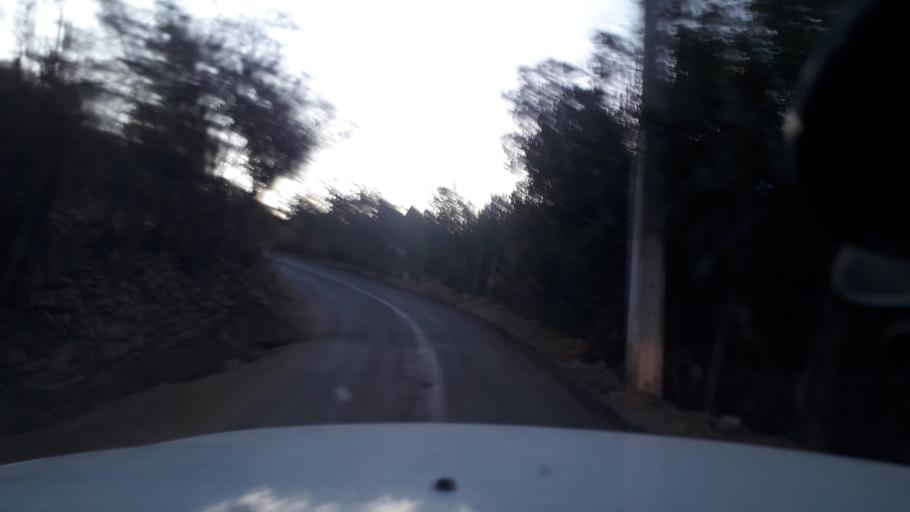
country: CL
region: Valparaiso
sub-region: Provincia de Marga Marga
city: Limache
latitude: -33.1802
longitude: -71.1142
